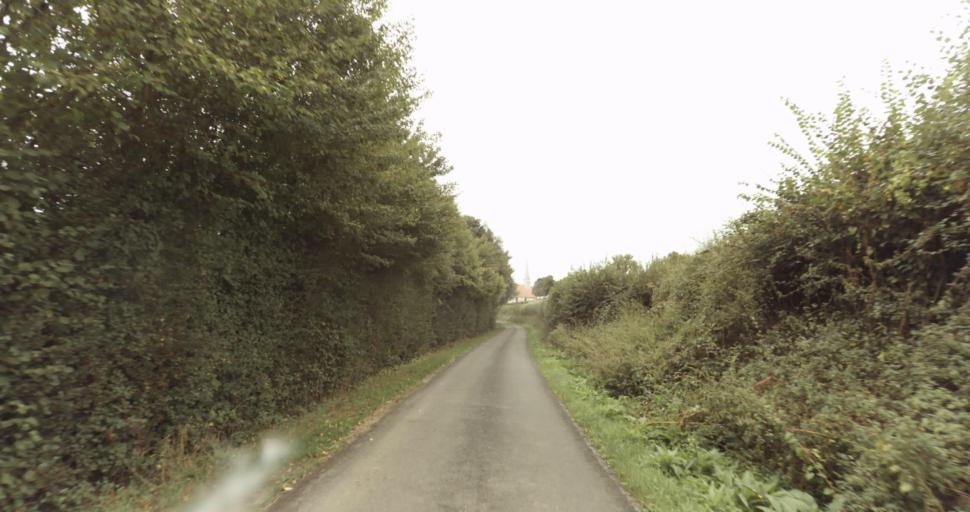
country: FR
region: Lower Normandy
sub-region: Departement de l'Orne
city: Gace
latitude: 48.8602
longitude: 0.2840
